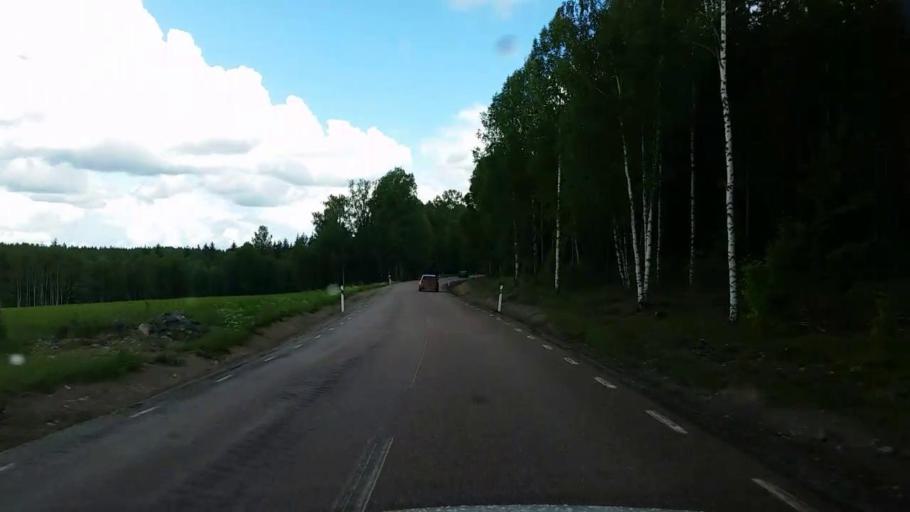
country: SE
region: Vaestmanland
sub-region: Skinnskattebergs Kommun
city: Skinnskatteberg
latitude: 59.8415
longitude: 15.8407
